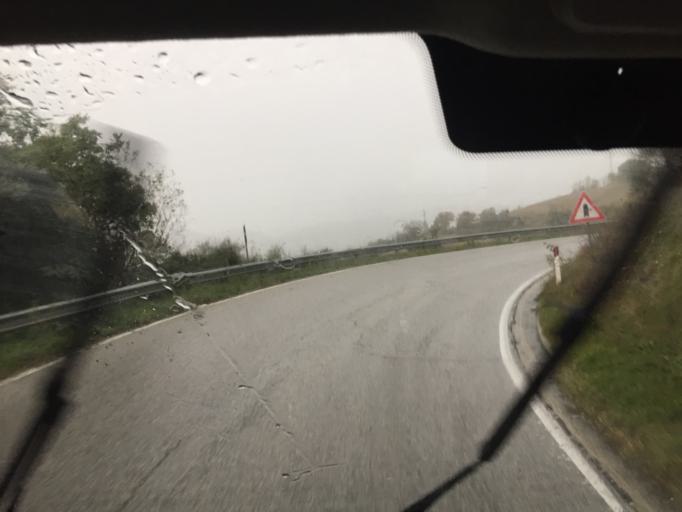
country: IT
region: The Marches
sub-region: Provincia di Macerata
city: Camerino
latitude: 43.1247
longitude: 13.0645
